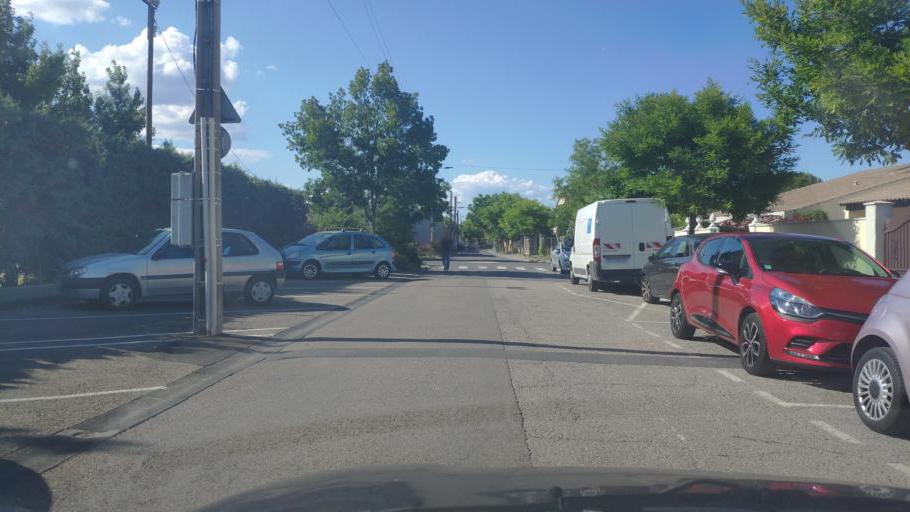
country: FR
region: Provence-Alpes-Cote d'Azur
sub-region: Departement du Vaucluse
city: Entraigues-sur-la-Sorgue
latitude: 43.9991
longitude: 4.9278
